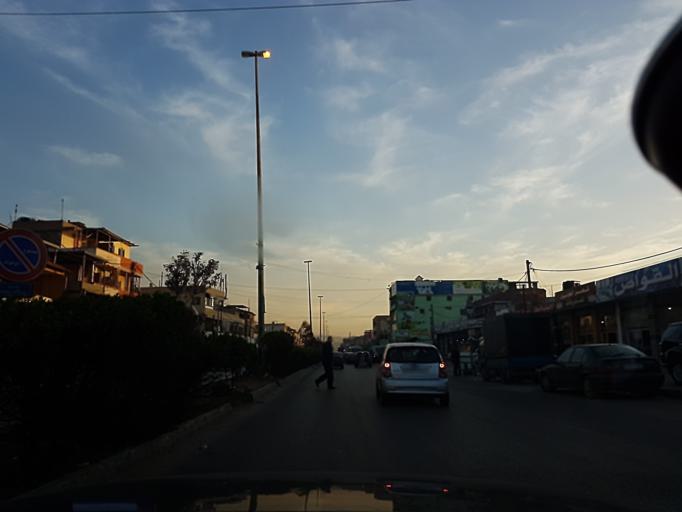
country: LB
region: Beyrouth
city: Beirut
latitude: 33.8419
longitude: 35.4848
